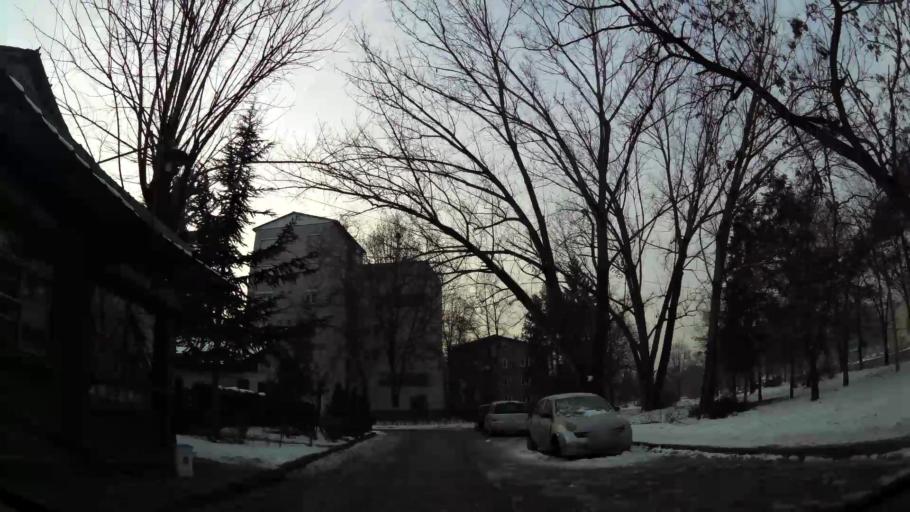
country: MK
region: Cair
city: Cair
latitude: 42.0224
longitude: 21.4447
